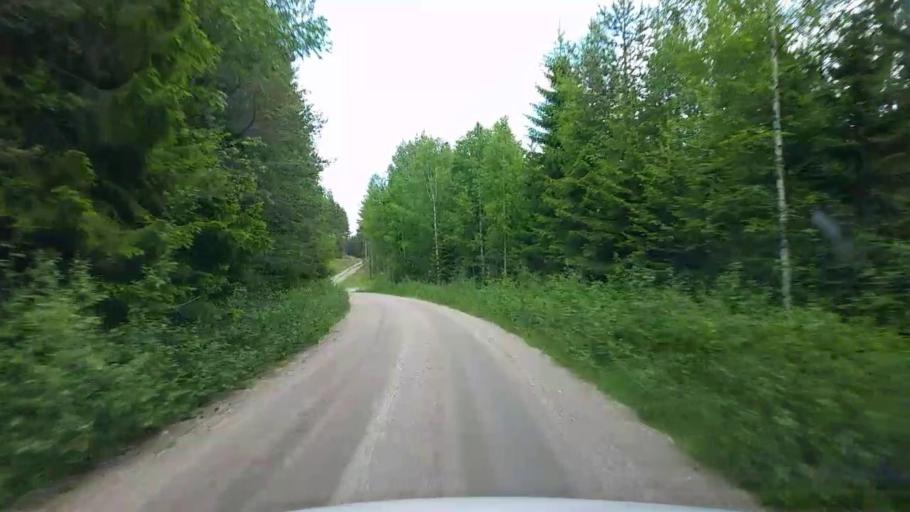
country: SE
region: Gaevleborg
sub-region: Ovanakers Kommun
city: Alfta
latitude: 61.5580
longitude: 15.9806
